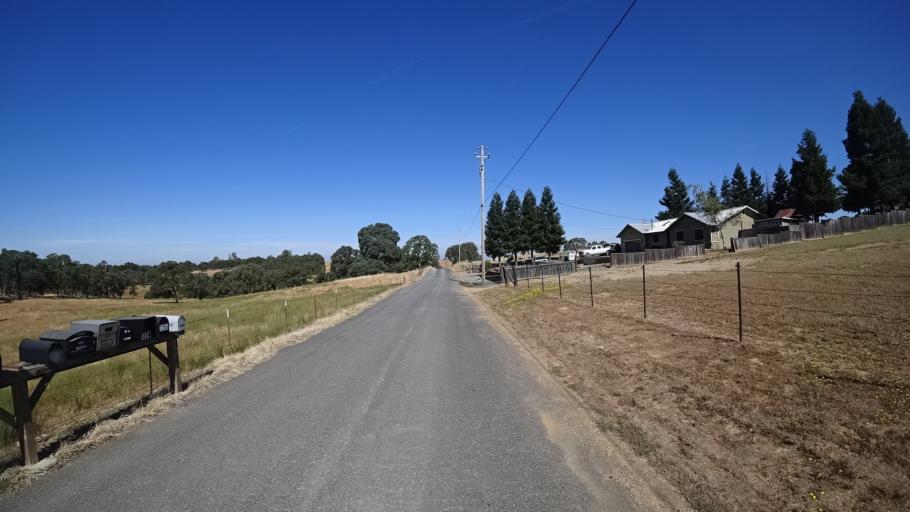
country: US
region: California
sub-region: Amador County
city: Jackson
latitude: 38.2586
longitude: -120.7670
